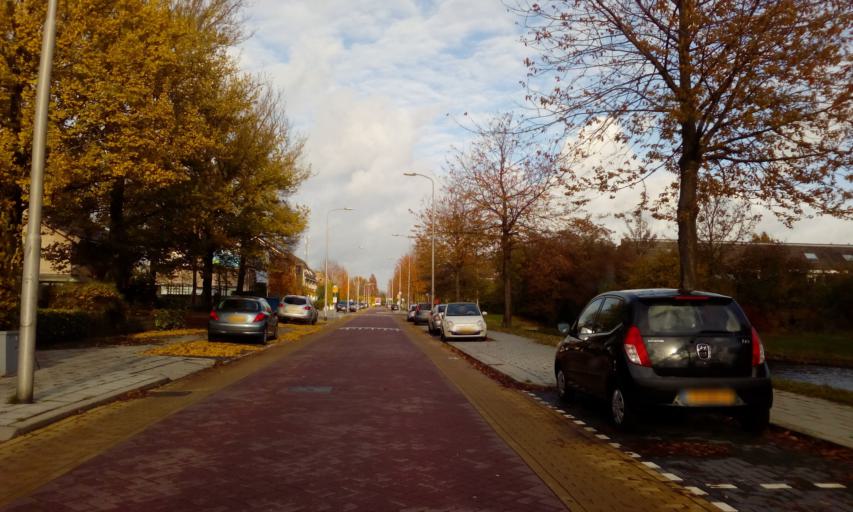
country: NL
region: South Holland
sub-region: Gemeente Lansingerland
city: Berkel en Rodenrijs
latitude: 52.0030
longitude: 4.4846
